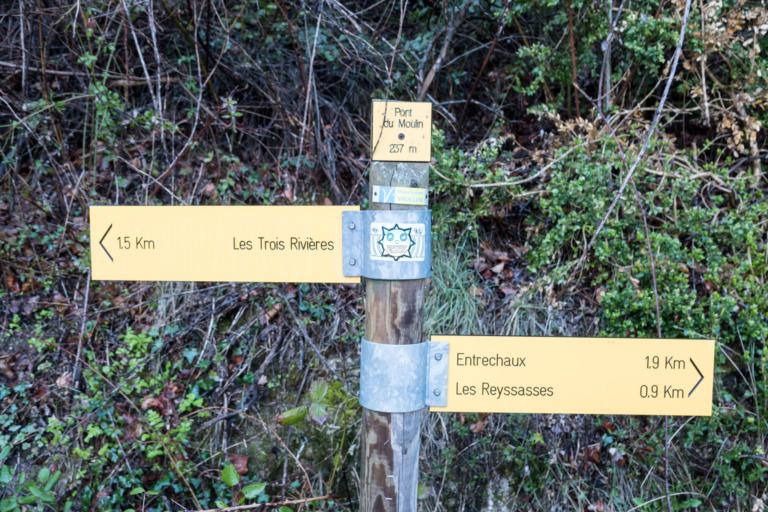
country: FR
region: Provence-Alpes-Cote d'Azur
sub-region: Departement du Vaucluse
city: Malaucene
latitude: 44.2291
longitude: 5.1370
